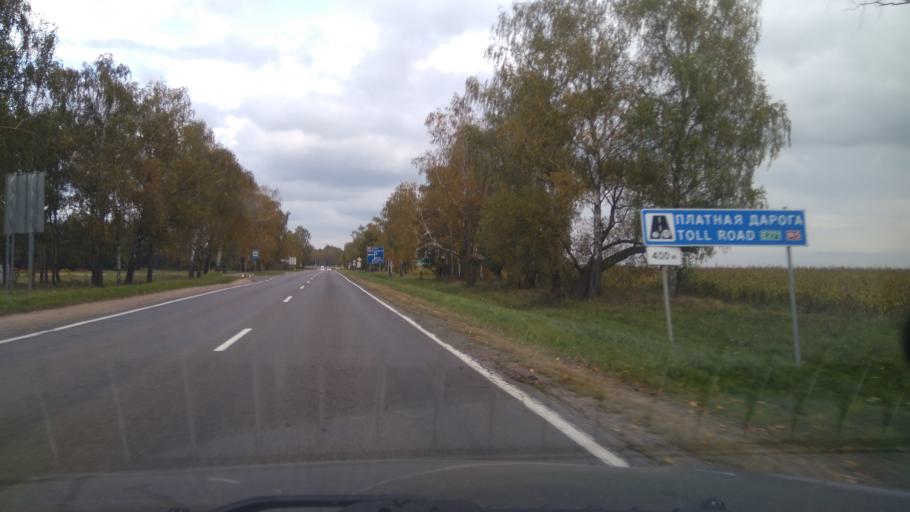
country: BY
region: Minsk
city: Svislach
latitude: 53.6545
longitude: 27.9365
